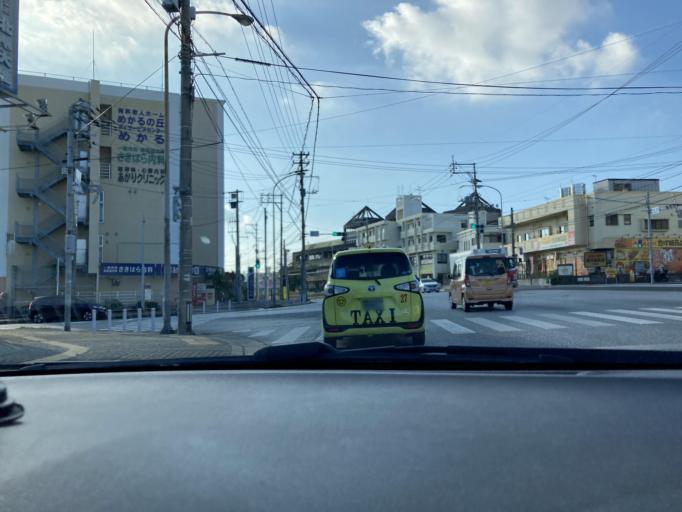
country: JP
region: Okinawa
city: Naha-shi
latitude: 26.2371
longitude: 127.6968
